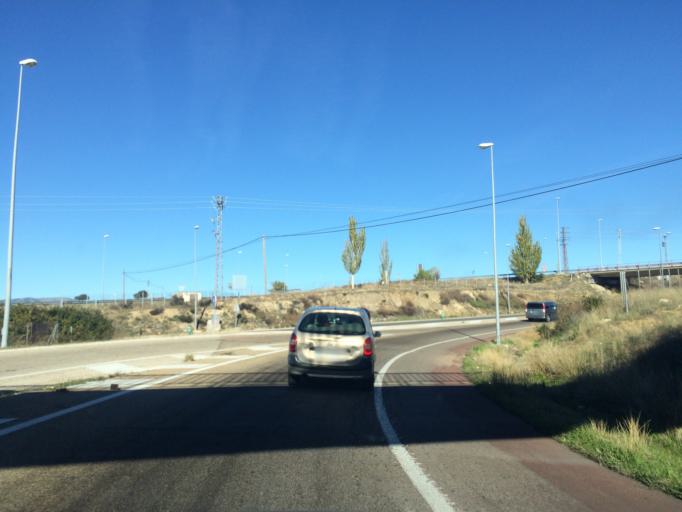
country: ES
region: Madrid
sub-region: Provincia de Madrid
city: Colmenar Viejo
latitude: 40.6841
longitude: -3.7864
